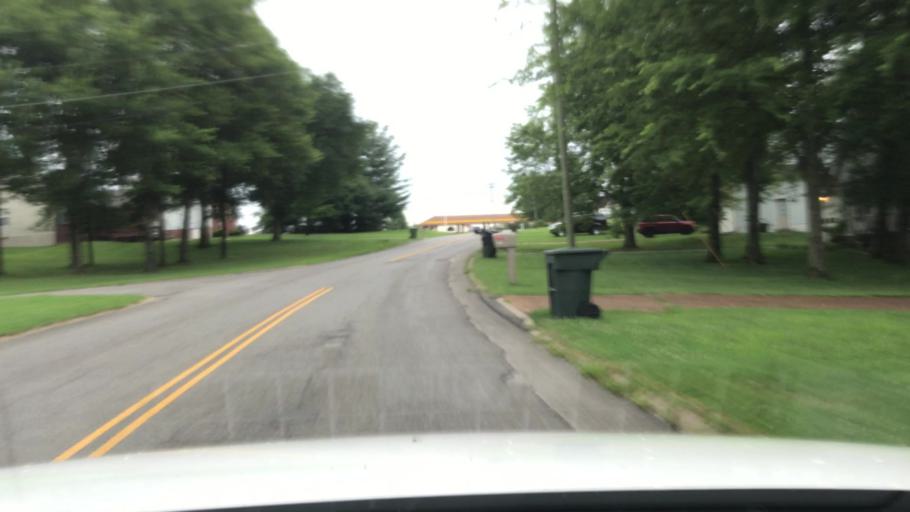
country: US
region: Tennessee
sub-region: Sumner County
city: Gallatin
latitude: 36.3722
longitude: -86.4662
